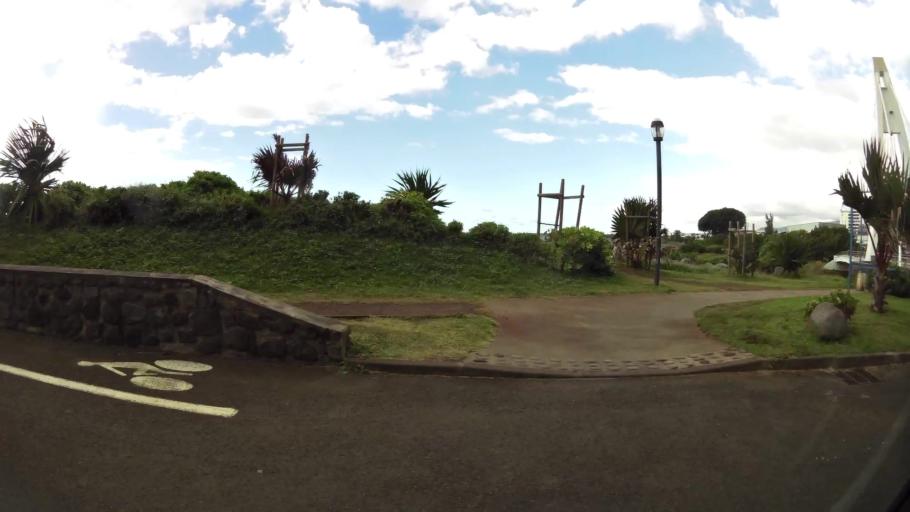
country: RE
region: Reunion
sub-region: Reunion
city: Saint-Denis
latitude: -20.8833
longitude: 55.4667
